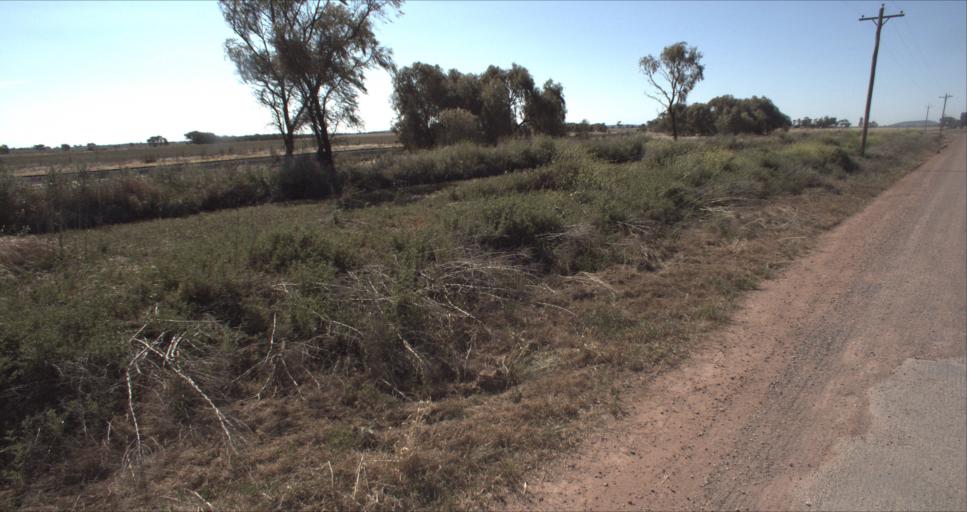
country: AU
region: New South Wales
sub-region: Leeton
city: Leeton
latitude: -34.4767
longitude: 146.3682
